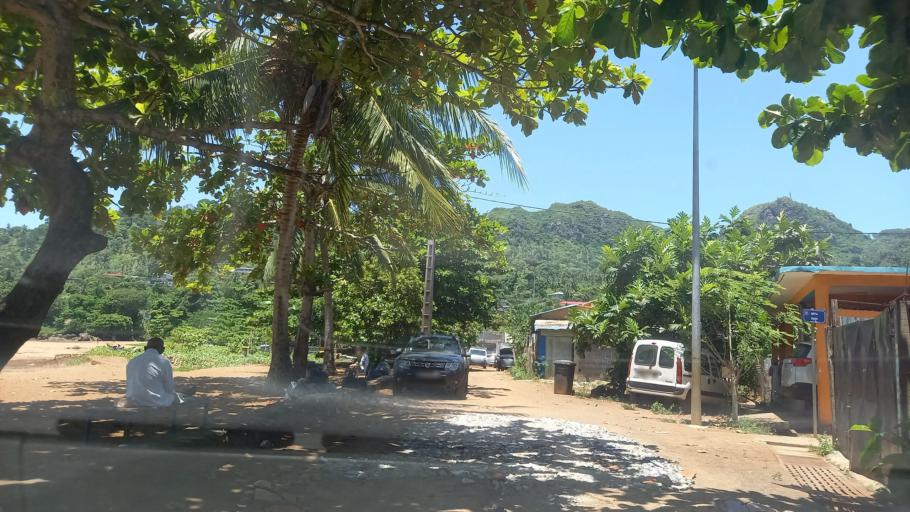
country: YT
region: Acoua
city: Acoua
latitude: -12.7257
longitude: 45.0570
